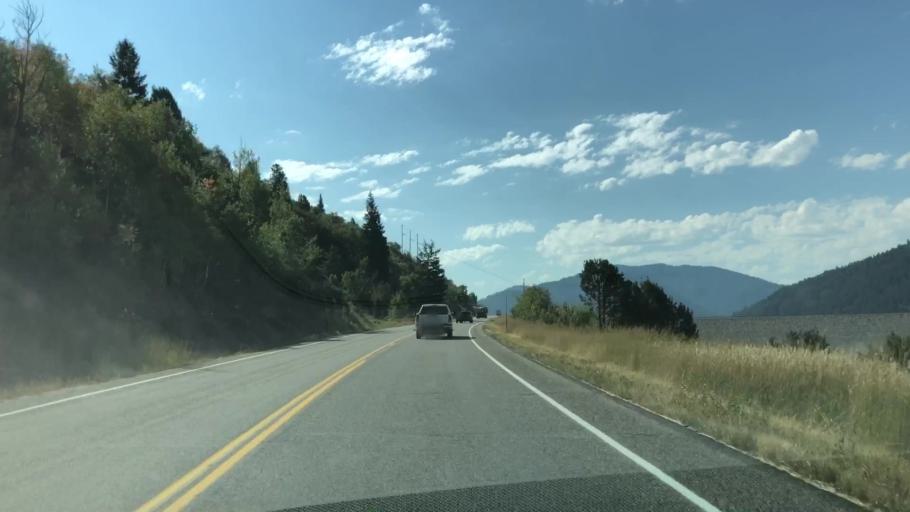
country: US
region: Idaho
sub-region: Teton County
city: Victor
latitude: 43.3395
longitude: -111.2006
